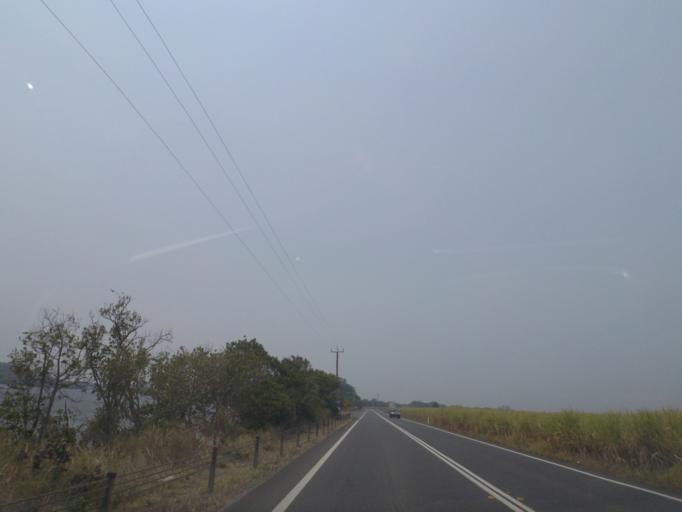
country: AU
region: New South Wales
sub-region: Richmond Valley
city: Evans Head
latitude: -28.9944
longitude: 153.4583
